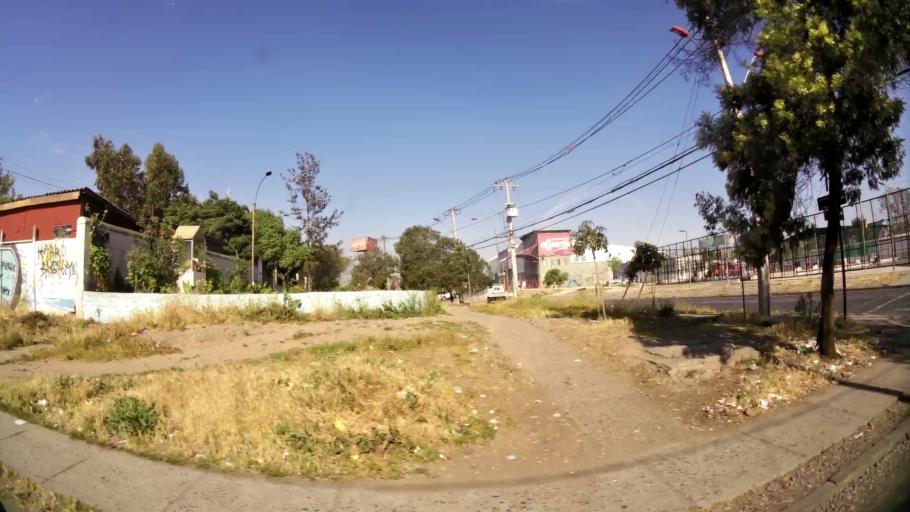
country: CL
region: Santiago Metropolitan
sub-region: Provincia de Santiago
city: Santiago
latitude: -33.5080
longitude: -70.6784
